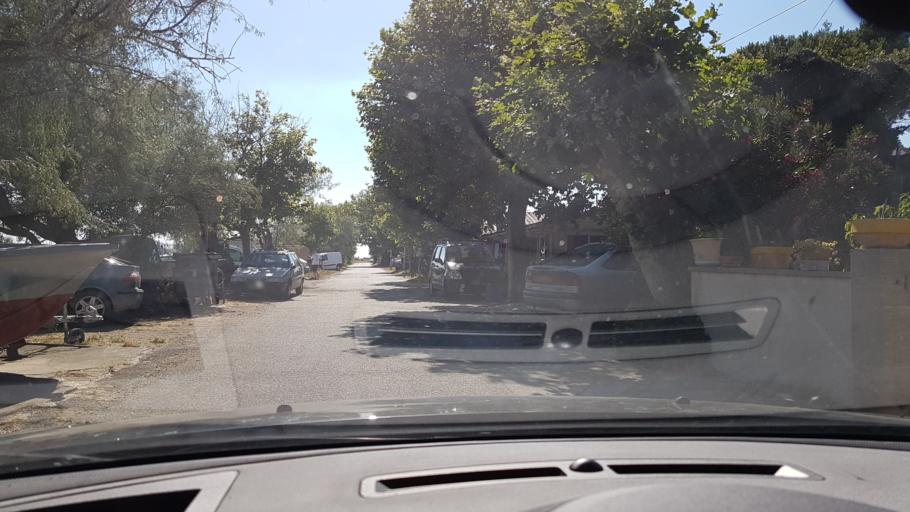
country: FR
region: Provence-Alpes-Cote d'Azur
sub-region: Departement des Bouches-du-Rhone
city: Port-Saint-Louis-du-Rhone
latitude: 43.3890
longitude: 4.8482
